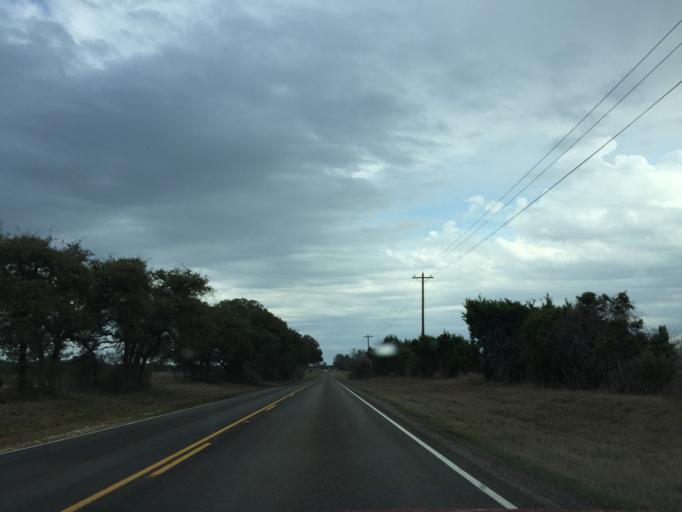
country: US
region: Texas
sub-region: Burnet County
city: Bertram
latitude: 30.6507
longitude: -97.9796
